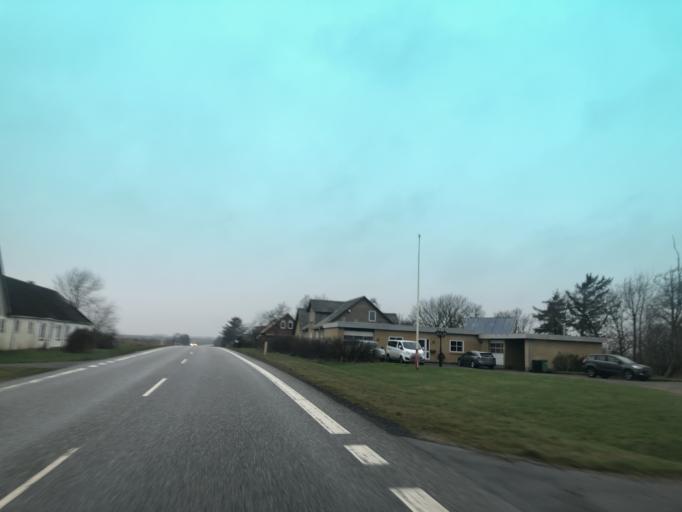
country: DK
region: North Denmark
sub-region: Thisted Kommune
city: Hurup
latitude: 56.6433
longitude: 8.4914
